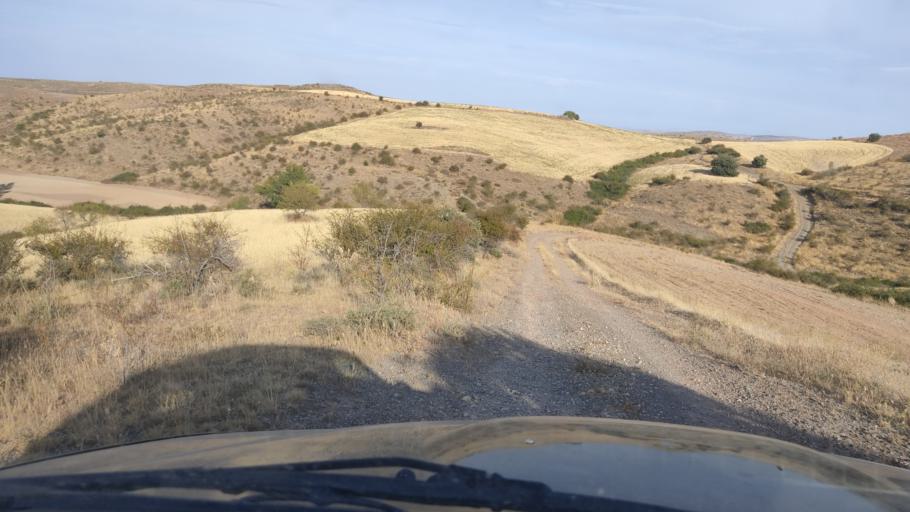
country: ES
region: Aragon
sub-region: Provincia de Teruel
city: Monforte de Moyuela
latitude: 41.0321
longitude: -1.0224
